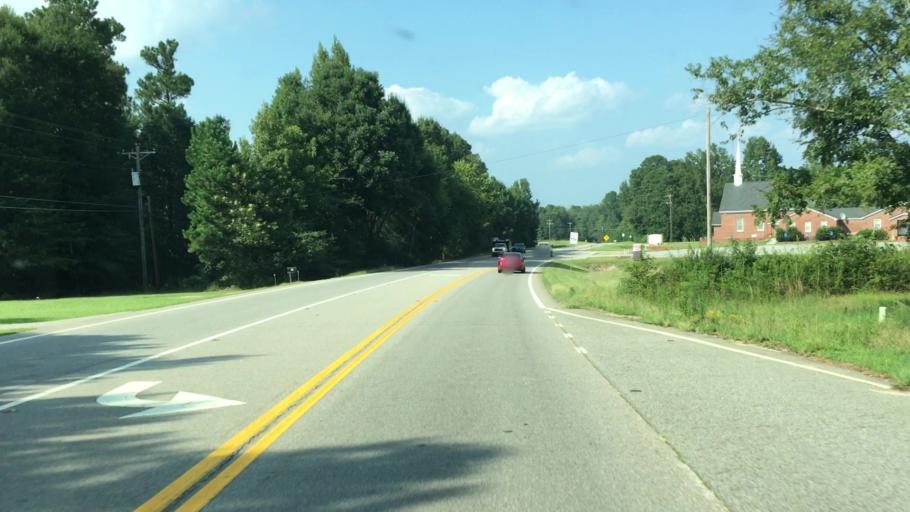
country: US
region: Georgia
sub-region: Walton County
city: Social Circle
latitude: 33.7138
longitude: -83.6988
